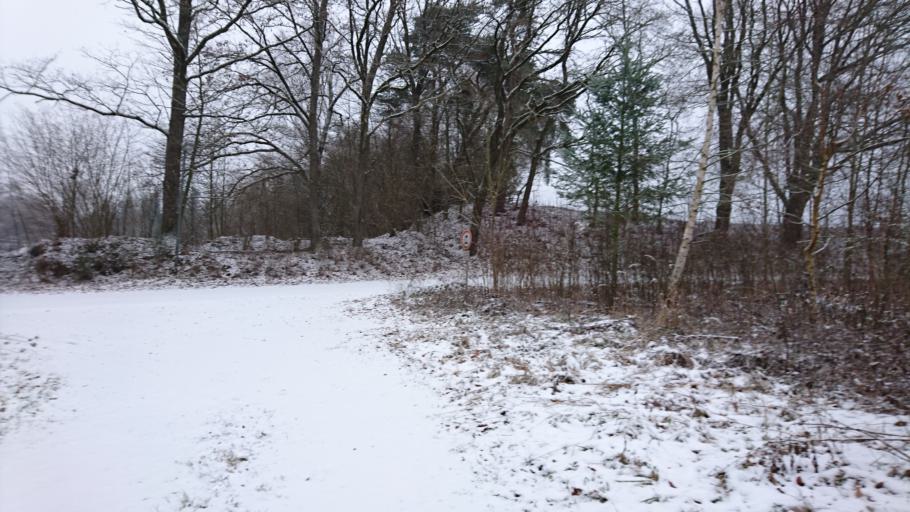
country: DE
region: Bavaria
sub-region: Swabia
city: Altenmunster
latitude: 48.4382
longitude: 10.6116
